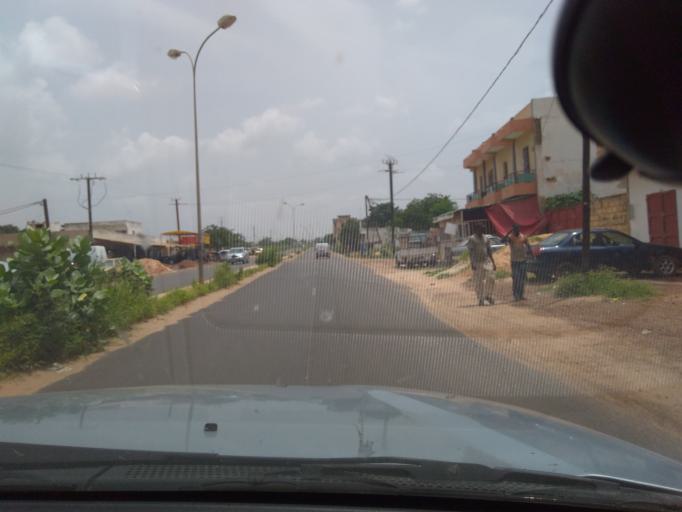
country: SN
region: Thies
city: Thies Nones
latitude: 14.7869
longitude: -16.9556
